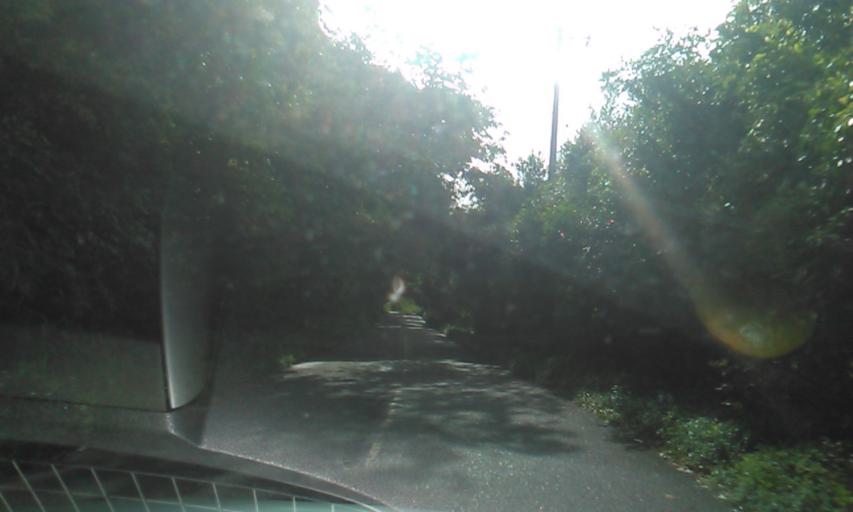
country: CO
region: Quindio
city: Cordoba
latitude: 4.4028
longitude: -75.7240
